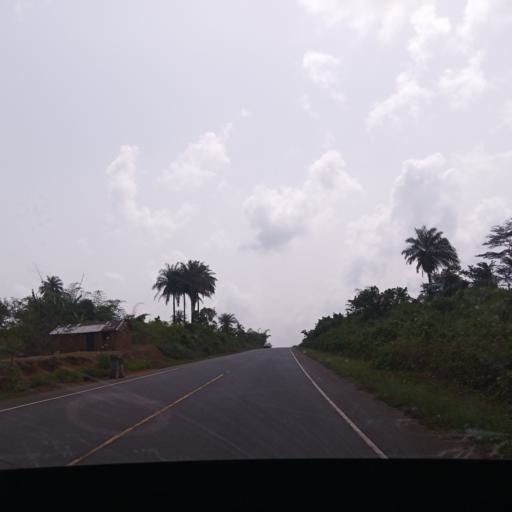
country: LR
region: Margibi
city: Kakata
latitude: 6.2394
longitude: -10.2846
